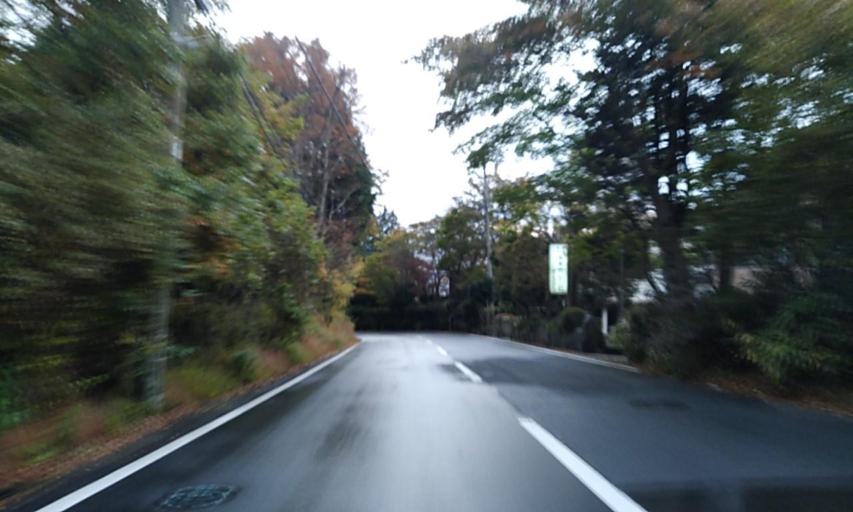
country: JP
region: Kanagawa
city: Hakone
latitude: 35.2465
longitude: 139.0072
